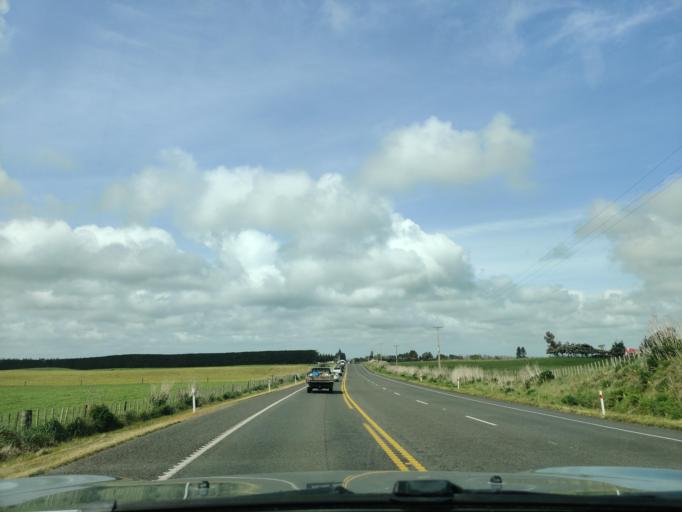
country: NZ
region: Taranaki
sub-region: South Taranaki District
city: Patea
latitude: -39.7659
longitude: 174.6146
